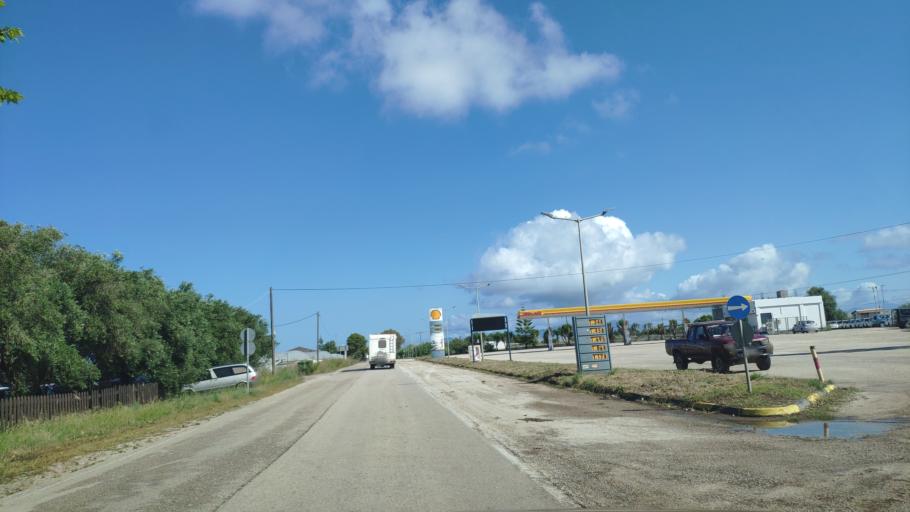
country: GR
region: Epirus
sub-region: Nomos Prevezis
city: Preveza
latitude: 38.9322
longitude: 20.7730
